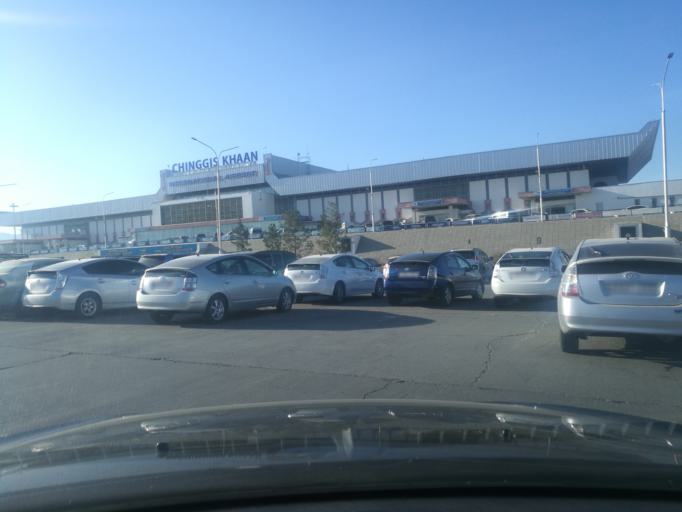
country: MN
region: Ulaanbaatar
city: Ulaanbaatar
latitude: 47.8537
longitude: 106.7633
